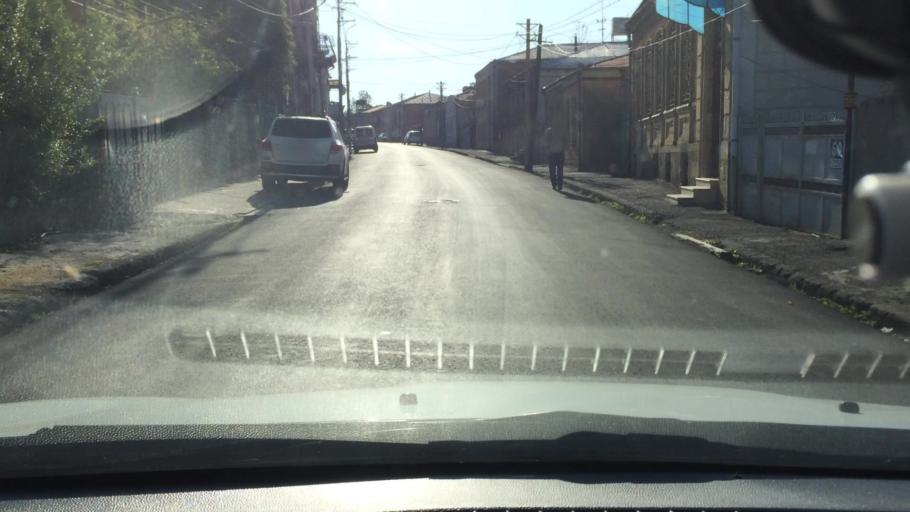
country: GE
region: Imereti
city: Kutaisi
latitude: 42.2702
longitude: 42.7112
